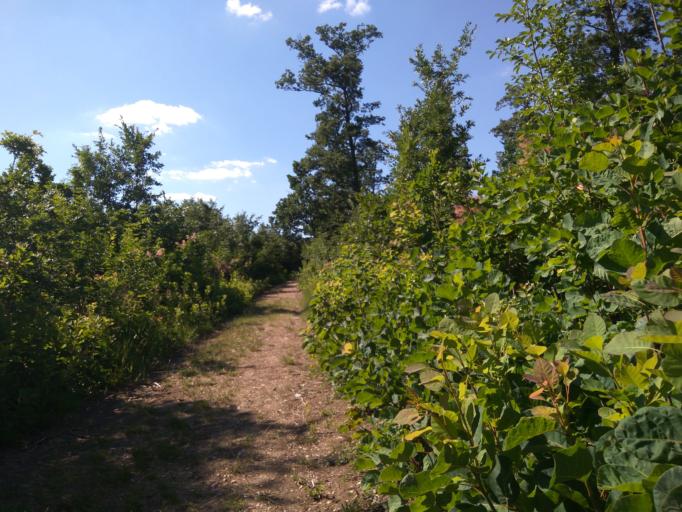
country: HU
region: Veszprem
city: Balatonfured
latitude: 46.9799
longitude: 17.8796
